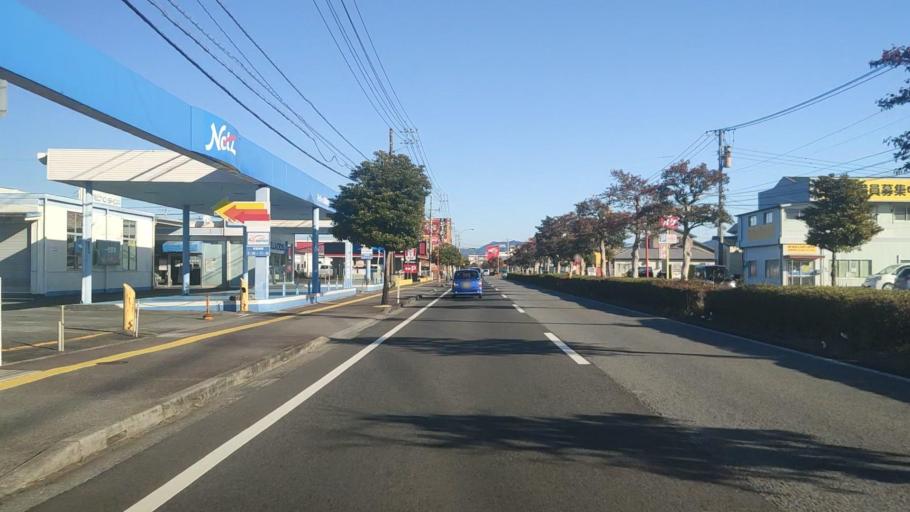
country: JP
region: Miyazaki
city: Nobeoka
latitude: 32.5648
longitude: 131.6822
